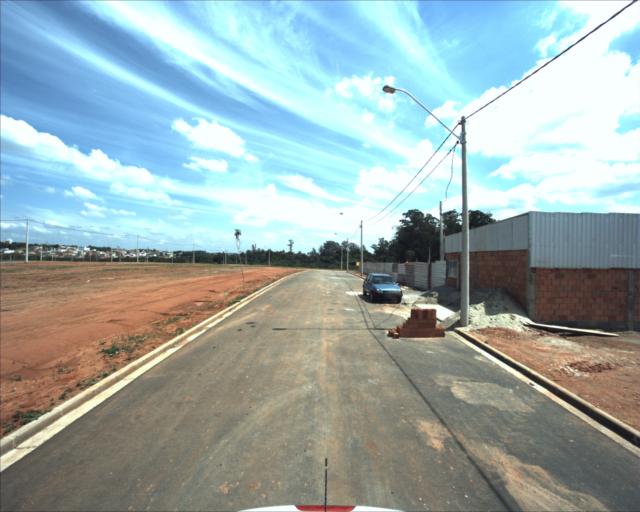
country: BR
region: Sao Paulo
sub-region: Sorocaba
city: Sorocaba
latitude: -23.4020
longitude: -47.4084
